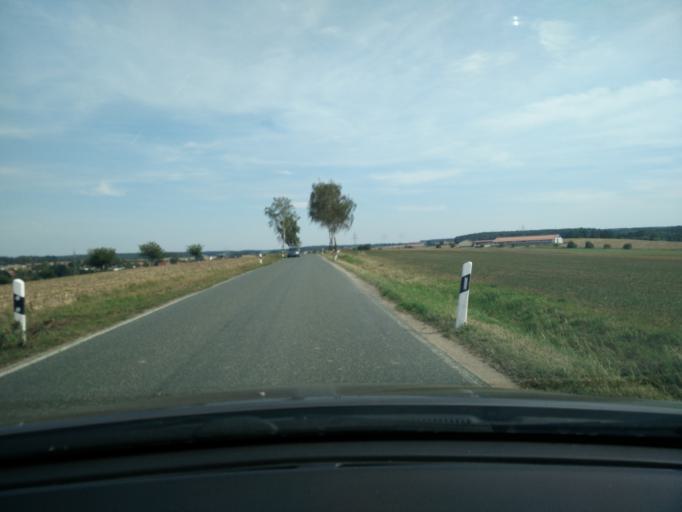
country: DE
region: Bavaria
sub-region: Regierungsbezirk Mittelfranken
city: Emskirchen
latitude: 49.5704
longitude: 10.6930
